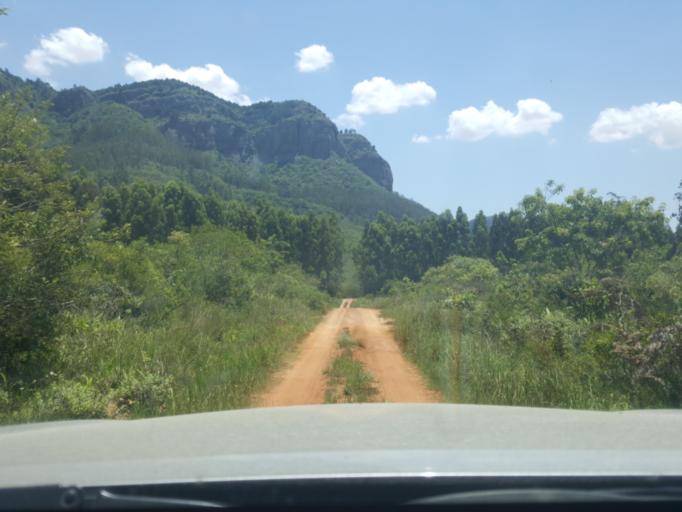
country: ZA
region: Limpopo
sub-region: Mopani District Municipality
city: Hoedspruit
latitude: -24.5963
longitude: 30.8550
